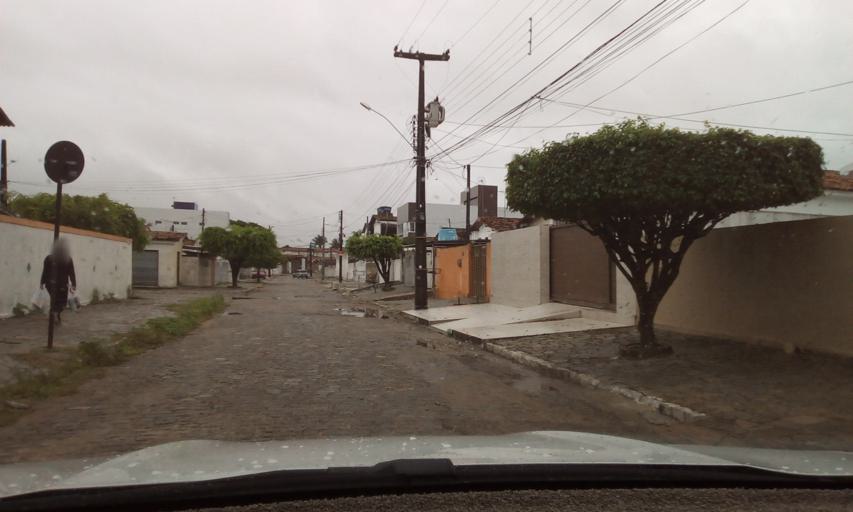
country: BR
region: Paraiba
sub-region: Conde
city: Conde
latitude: -7.2042
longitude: -34.8475
